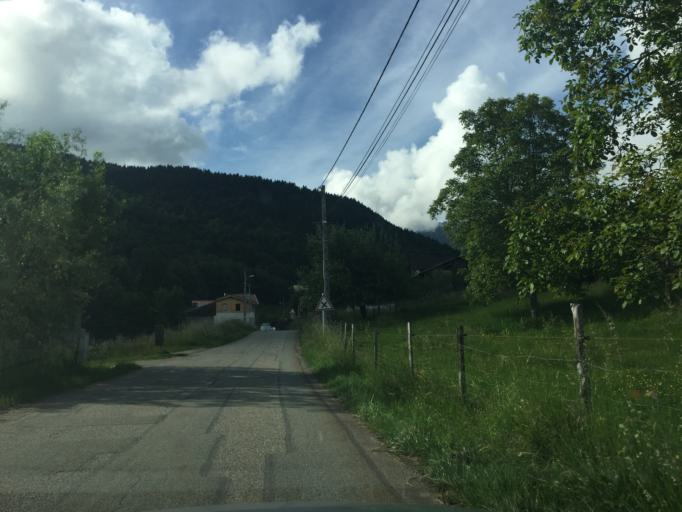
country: FR
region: Rhone-Alpes
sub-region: Departement de la Savoie
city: La Rochette
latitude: 45.4416
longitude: 6.1393
